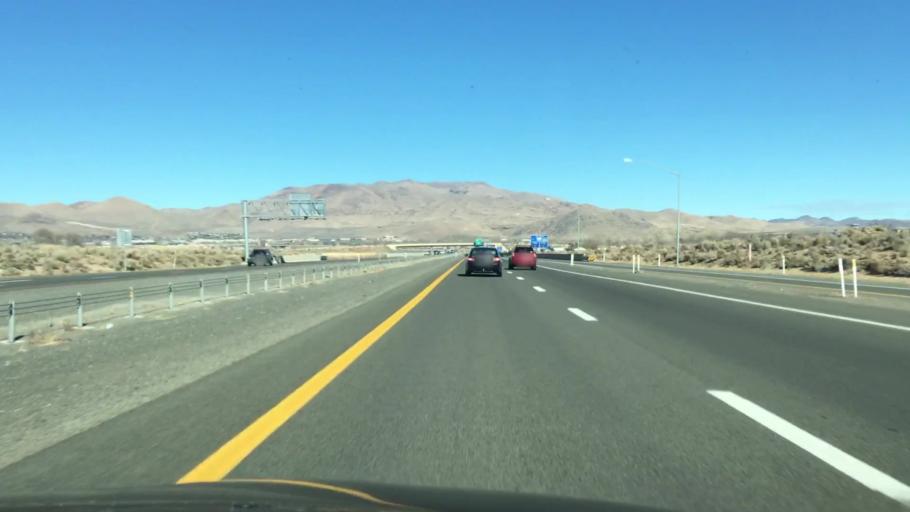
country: US
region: Nevada
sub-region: Carson City
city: Carson City
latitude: 39.1539
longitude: -119.7435
